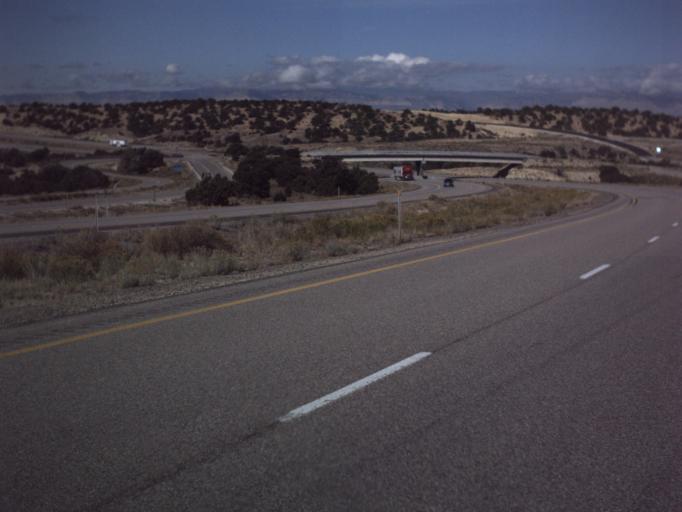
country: US
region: Utah
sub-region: Emery County
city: Ferron
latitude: 38.8540
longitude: -110.9093
